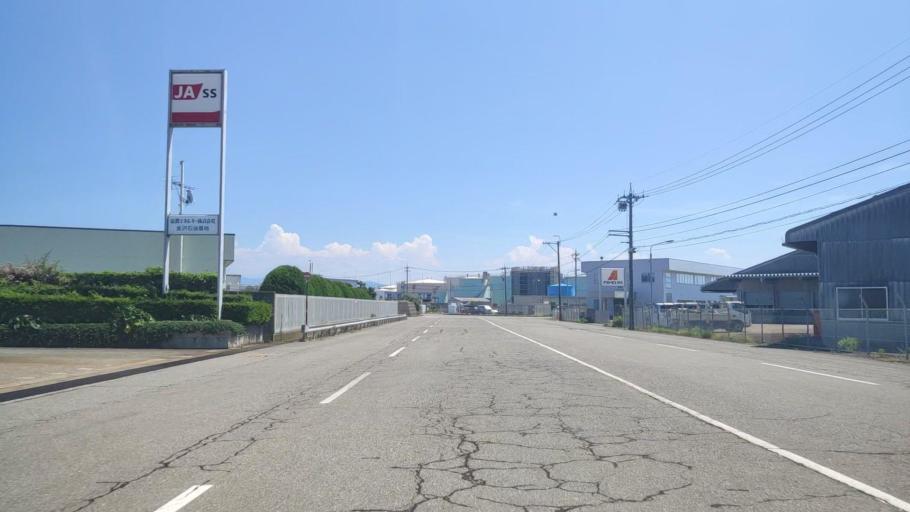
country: JP
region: Ishikawa
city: Kanazawa-shi
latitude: 36.6236
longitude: 136.6095
